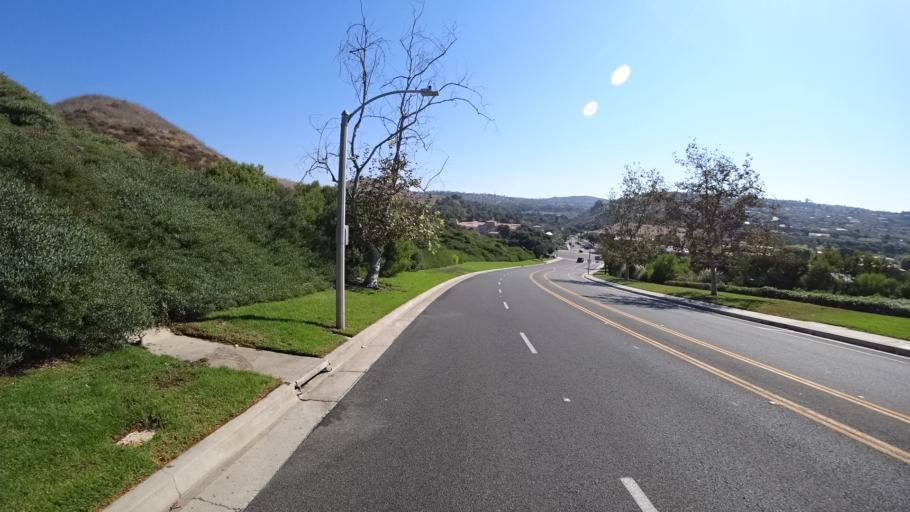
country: US
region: California
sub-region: Orange County
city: San Clemente
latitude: 33.4427
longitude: -117.6180
